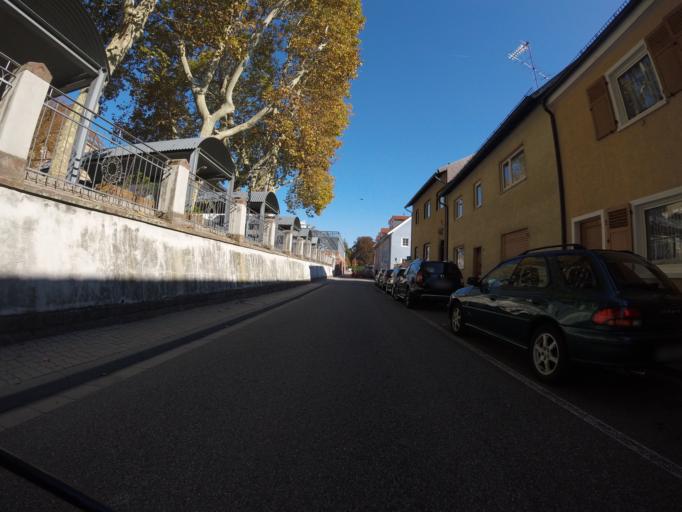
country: DE
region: Rheinland-Pfalz
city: Speyer
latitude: 49.3146
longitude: 8.4410
